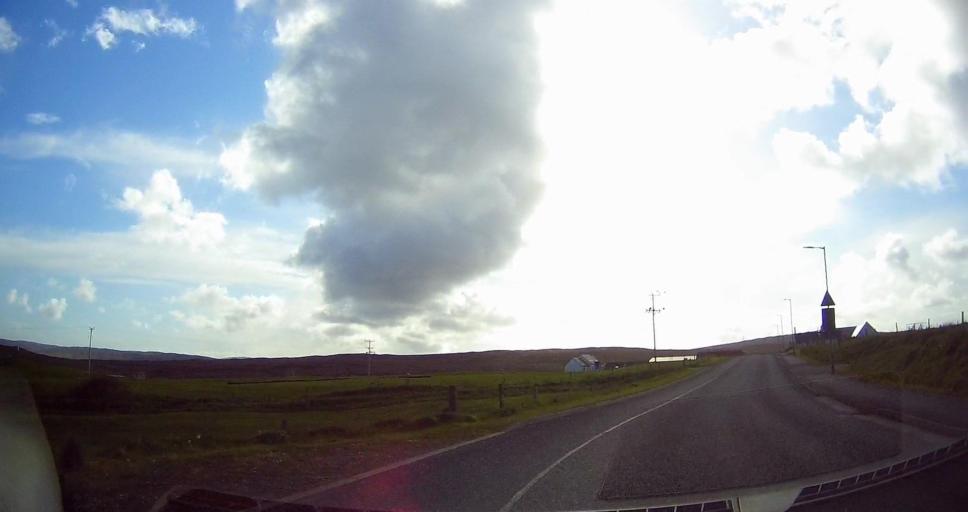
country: GB
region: Scotland
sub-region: Shetland Islands
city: Shetland
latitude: 60.3690
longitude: -1.1367
